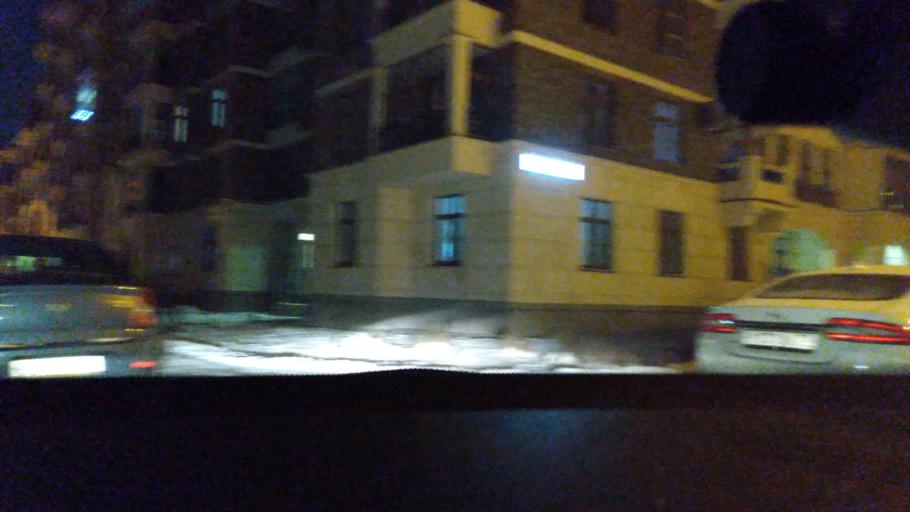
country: RU
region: Moskovskaya
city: Opalikha
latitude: 55.8153
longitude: 37.2458
